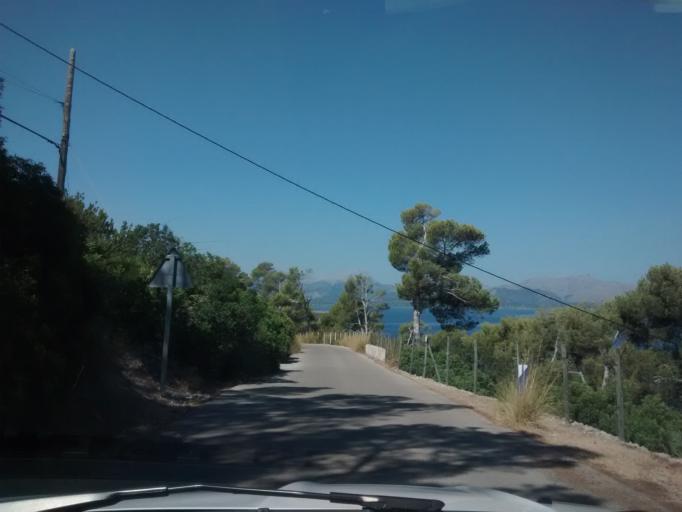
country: ES
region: Balearic Islands
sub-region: Illes Balears
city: Port d'Alcudia
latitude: 39.8751
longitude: 3.1690
